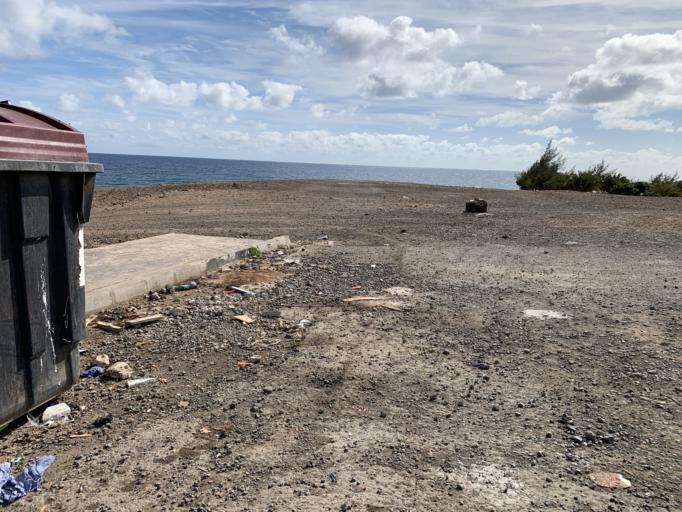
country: ES
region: Canary Islands
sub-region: Provincia de Las Palmas
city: Puerto del Rosario
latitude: 28.5016
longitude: -13.8481
